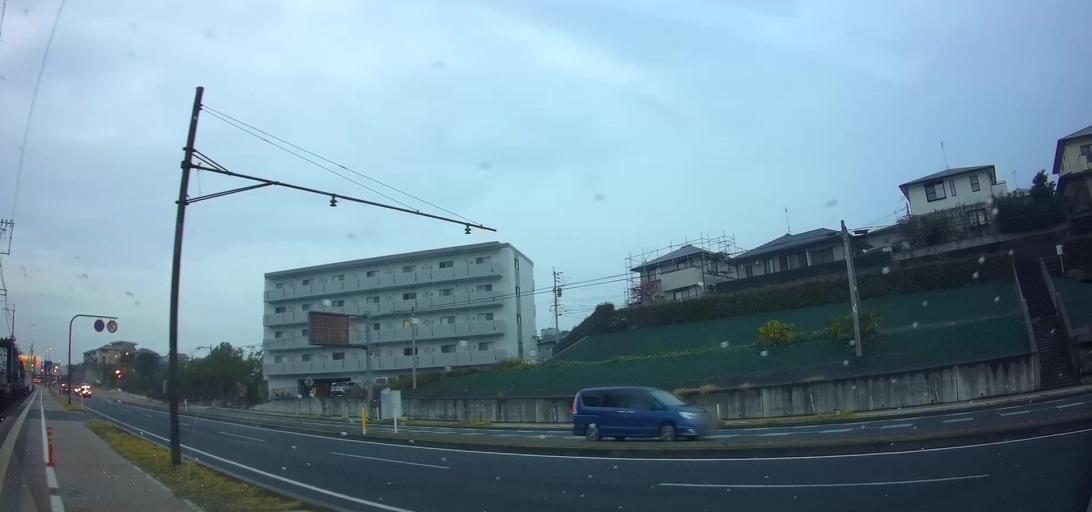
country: JP
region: Nagasaki
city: Omura
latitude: 32.8918
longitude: 129.9696
